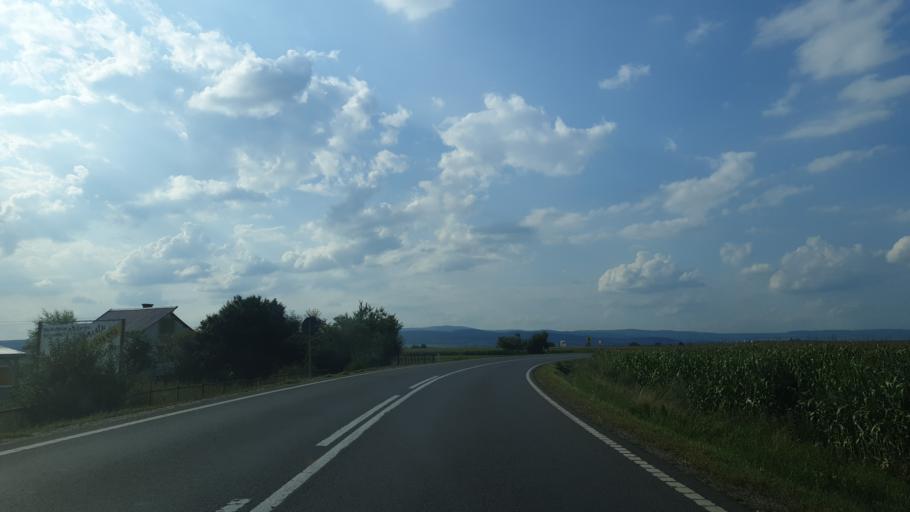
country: RO
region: Covasna
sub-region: Comuna Chichis
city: Chichis
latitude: 45.7801
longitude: 25.8068
